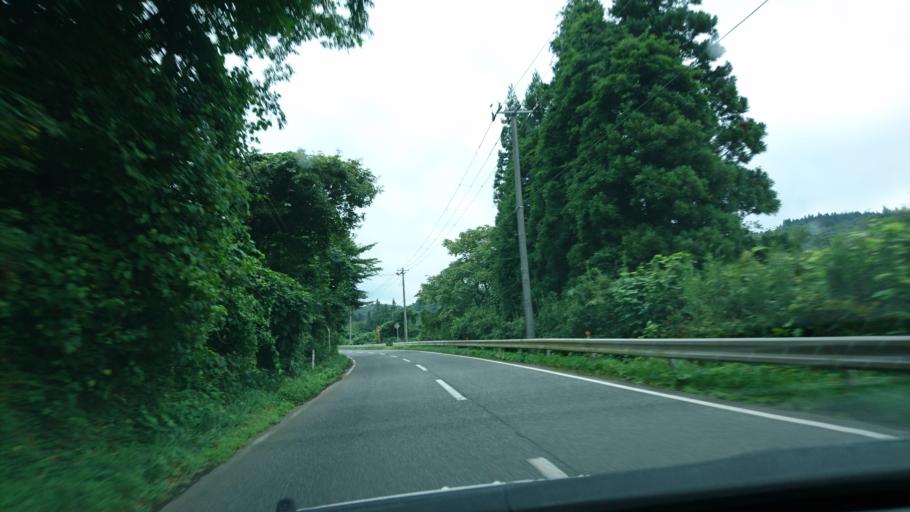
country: JP
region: Iwate
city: Ichinoseki
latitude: 38.9101
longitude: 141.0590
